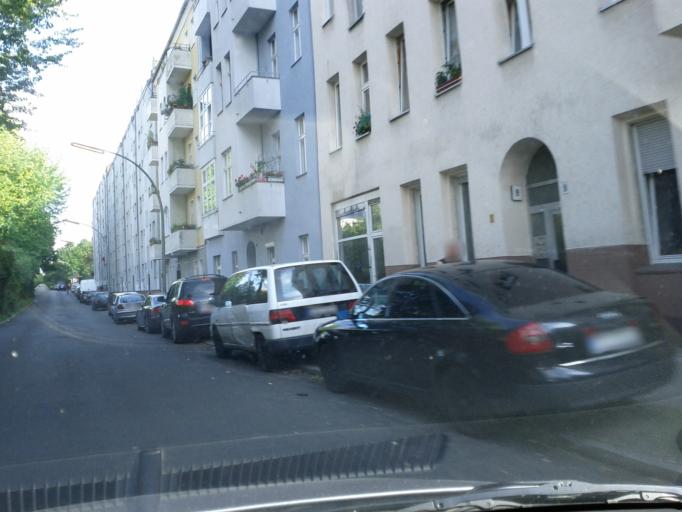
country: DE
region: Berlin
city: Berlin Treptow
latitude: 52.4857
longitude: 13.4423
